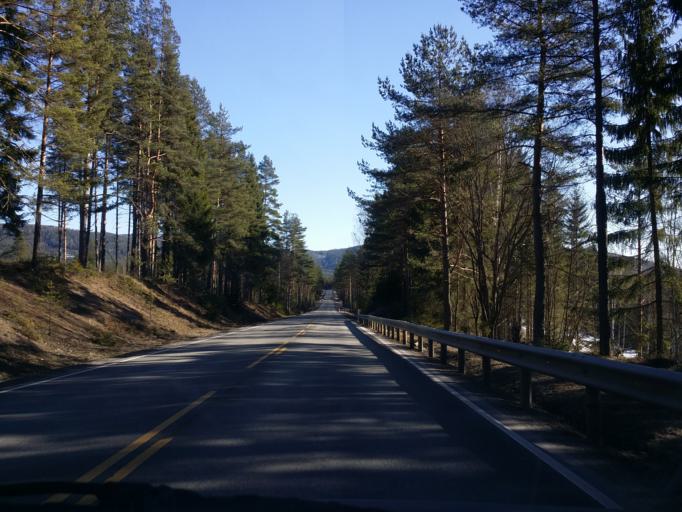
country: NO
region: Buskerud
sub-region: Ringerike
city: Honefoss
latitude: 60.3046
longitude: 10.1659
